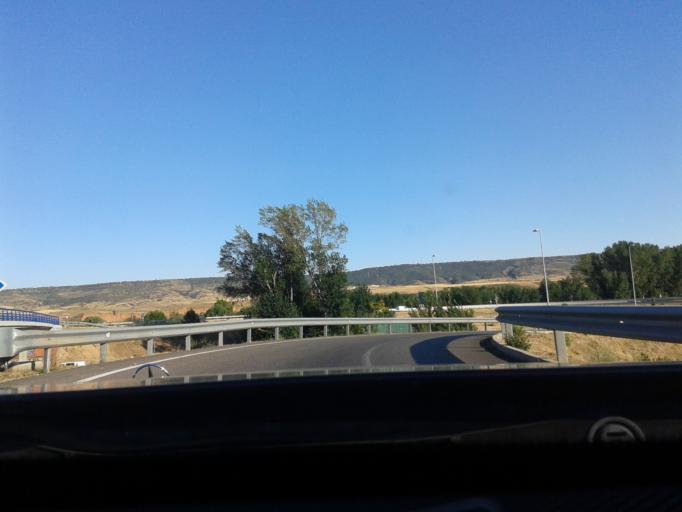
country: ES
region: Castille-La Mancha
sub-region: Provincia de Guadalajara
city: Azuqueca de Henares
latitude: 40.5703
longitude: -3.2469
